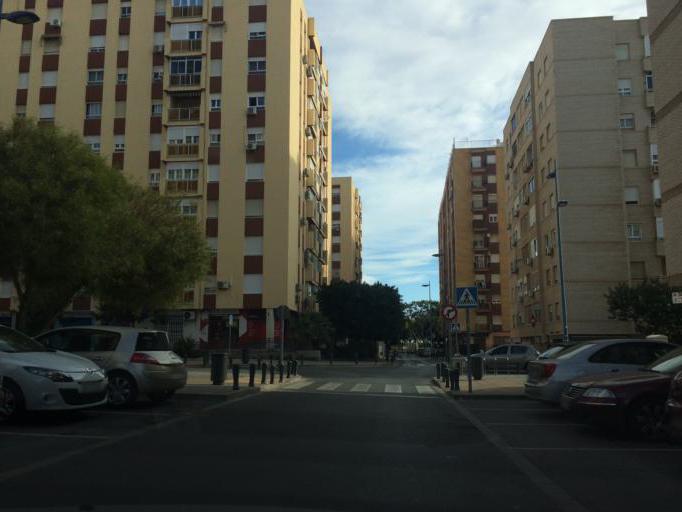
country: ES
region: Andalusia
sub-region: Provincia de Almeria
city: Almeria
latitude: 36.8419
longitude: -2.4491
